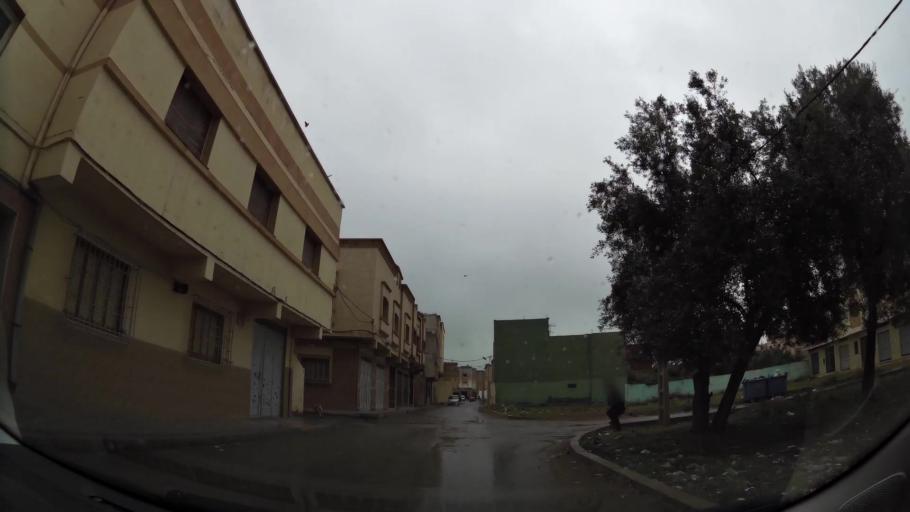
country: MA
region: Oriental
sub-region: Nador
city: Nador
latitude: 35.1622
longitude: -2.9536
